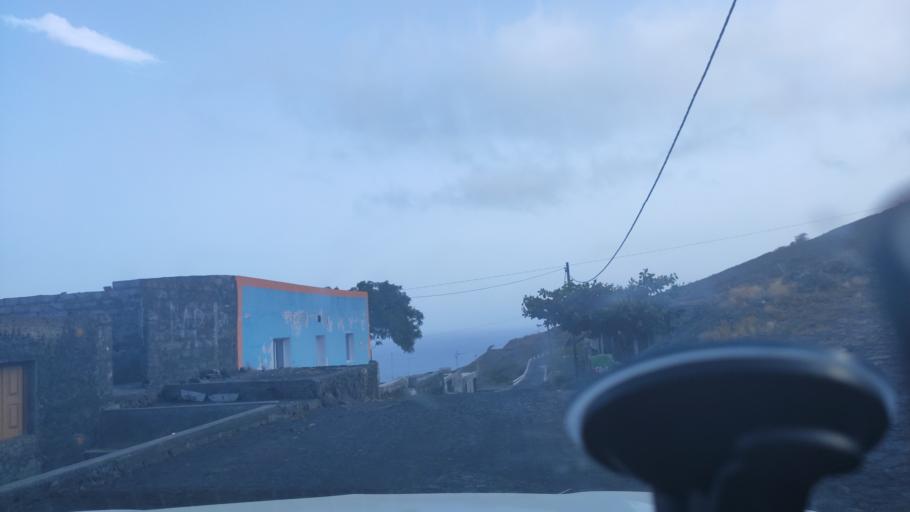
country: CV
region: Mosteiros
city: Porto dos Mosteiros
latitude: 15.0053
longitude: -24.3038
